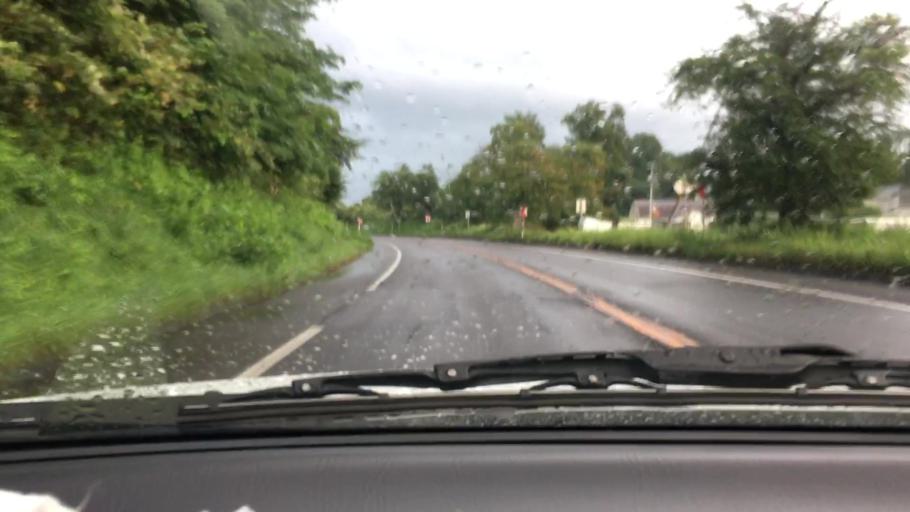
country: JP
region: Hokkaido
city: Nanae
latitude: 42.0832
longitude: 140.5864
